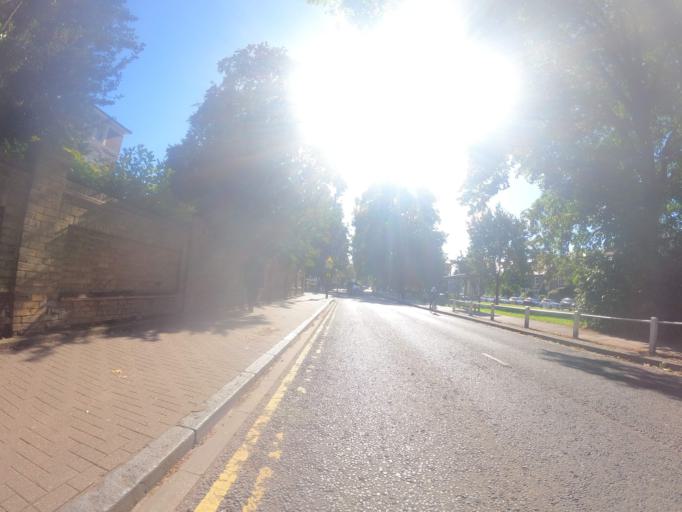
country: GB
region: England
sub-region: Greater London
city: Ealing
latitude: 51.5097
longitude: -0.3055
